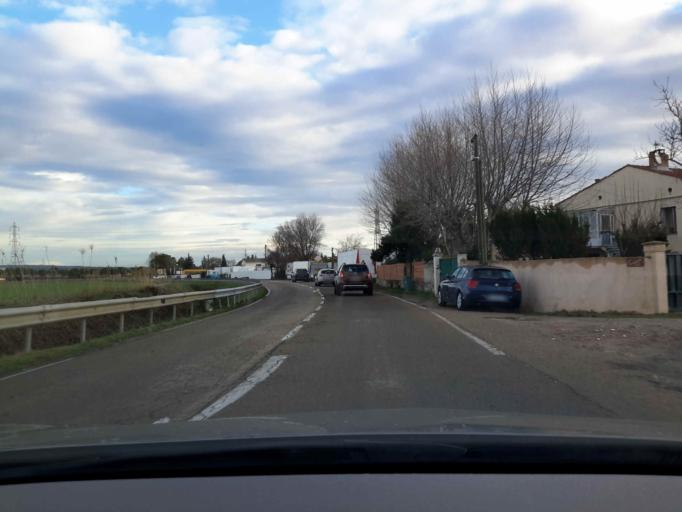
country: FR
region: Languedoc-Roussillon
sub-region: Departement du Gard
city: Caissargues
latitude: 43.7935
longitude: 4.3516
